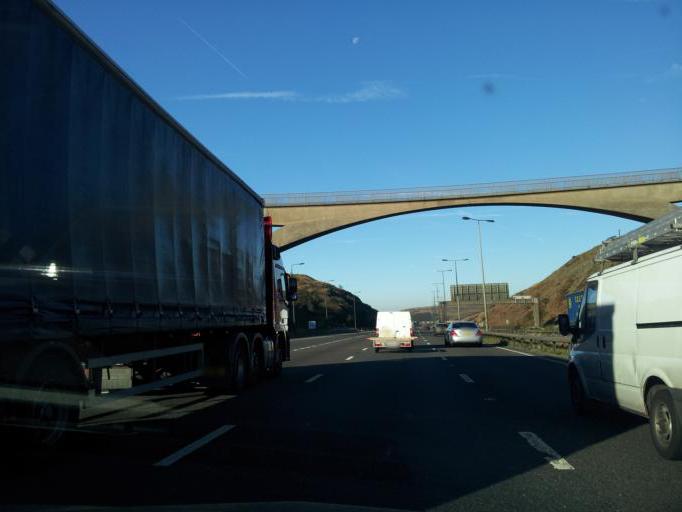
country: GB
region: England
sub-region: Borough of Oldham
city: Delph
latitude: 53.6293
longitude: -2.0257
